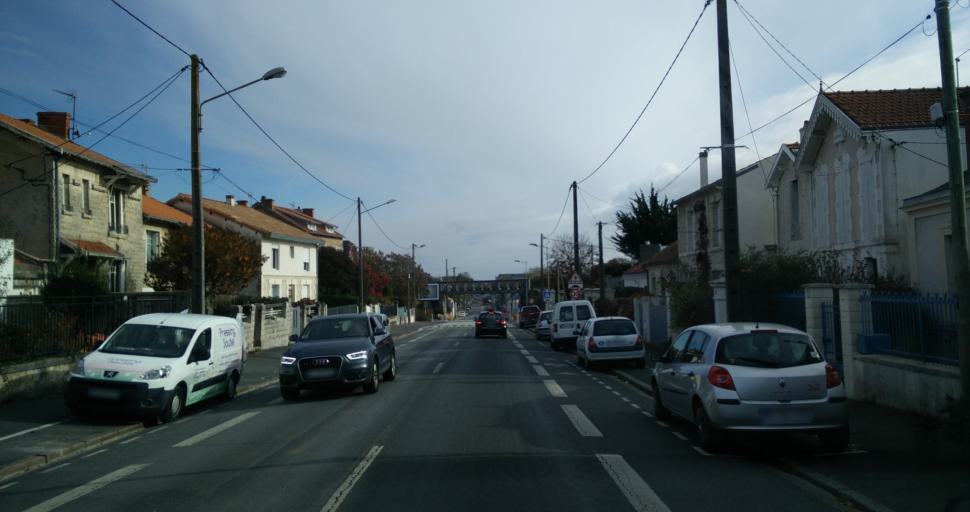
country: FR
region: Poitou-Charentes
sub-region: Departement de la Charente-Maritime
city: La Rochelle
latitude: 46.1638
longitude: -1.1724
